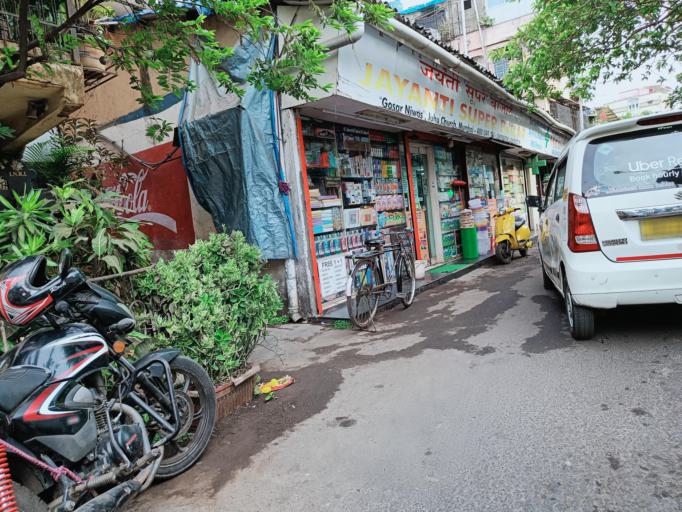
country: IN
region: Maharashtra
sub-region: Mumbai Suburban
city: Mumbai
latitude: 19.1112
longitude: 72.8267
